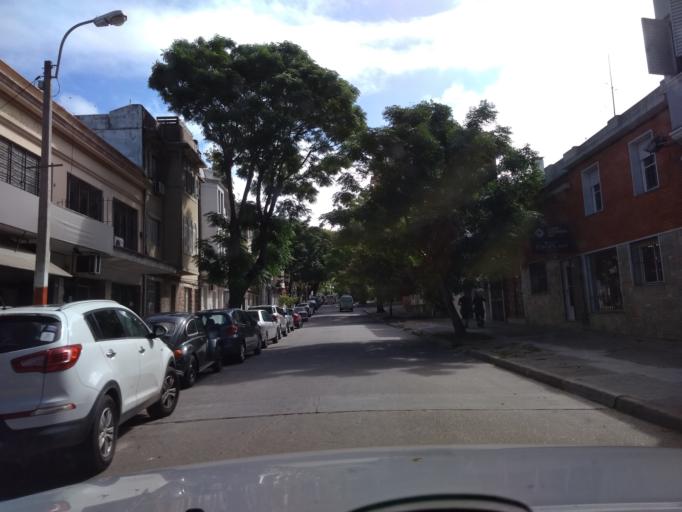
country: UY
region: Montevideo
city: Montevideo
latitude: -34.9063
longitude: -56.1563
